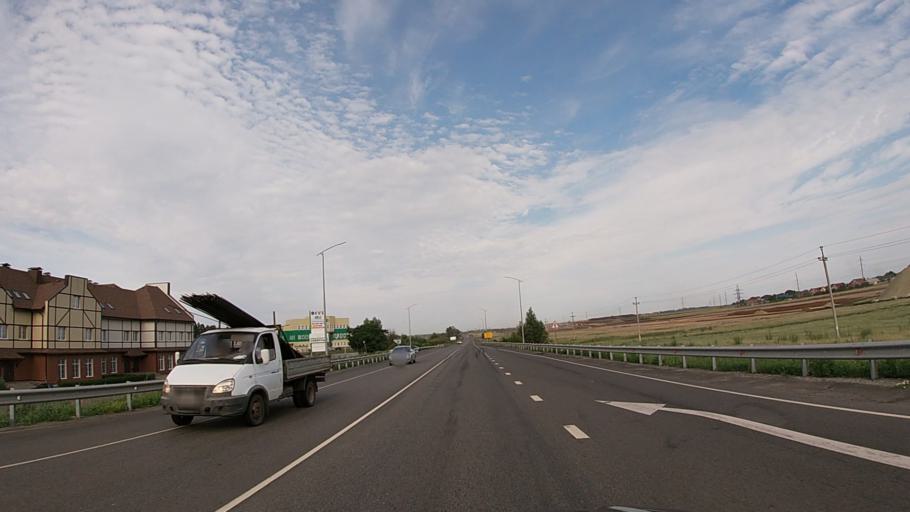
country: RU
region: Belgorod
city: Severnyy
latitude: 50.6673
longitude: 36.5544
